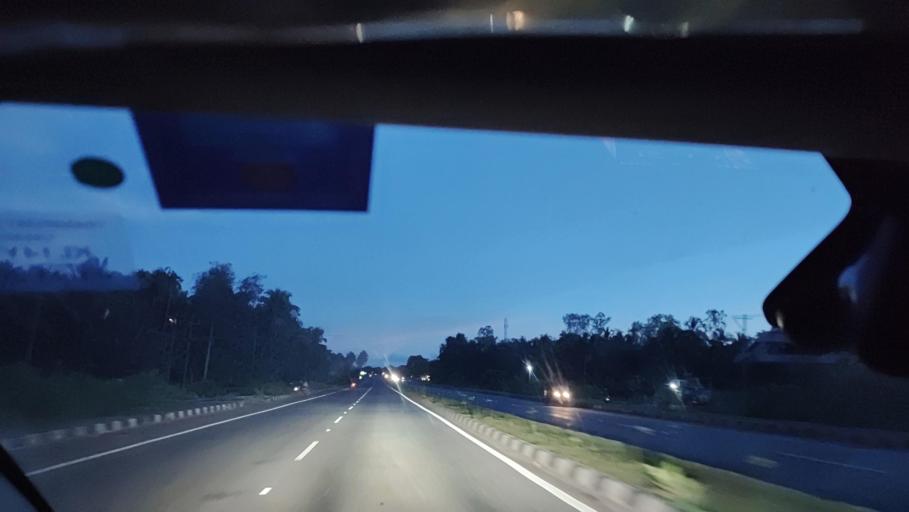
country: IN
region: Karnataka
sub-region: Uttar Kannada
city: Gokarna
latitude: 14.5522
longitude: 74.3925
